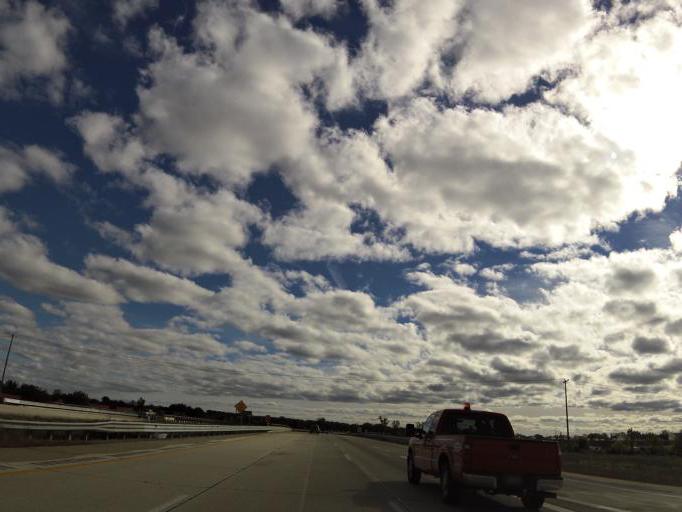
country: US
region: Michigan
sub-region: Genesee County
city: Davison
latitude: 43.0164
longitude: -83.5572
